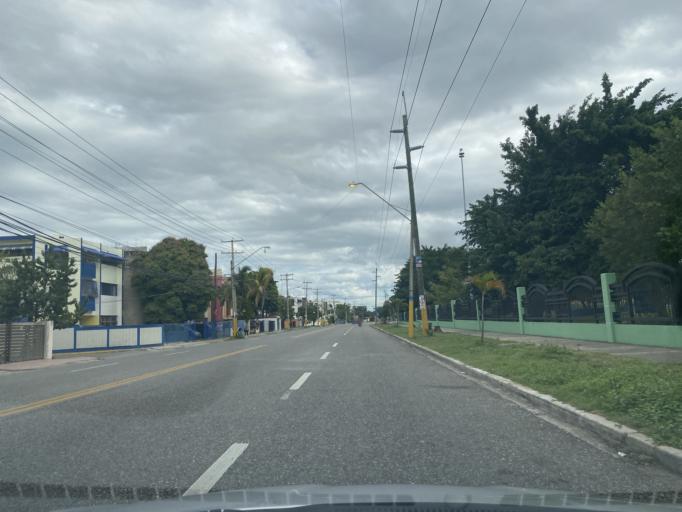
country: DO
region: Santo Domingo
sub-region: Santo Domingo
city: Santo Domingo Este
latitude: 18.4814
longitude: -69.8517
